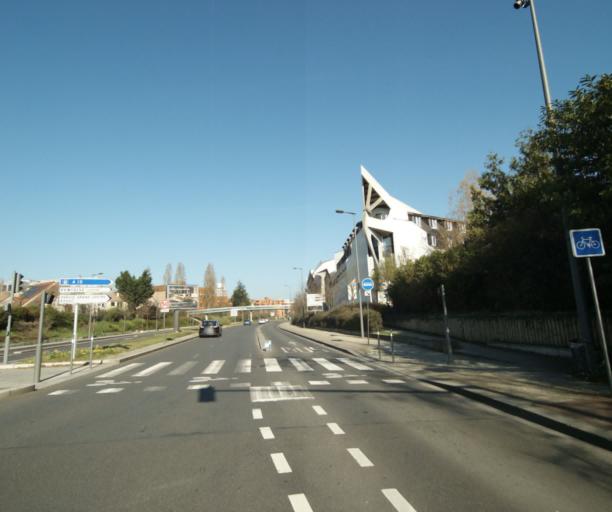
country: FR
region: Ile-de-France
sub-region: Departement du Val-d'Oise
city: Cergy
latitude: 49.0305
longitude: 2.0708
